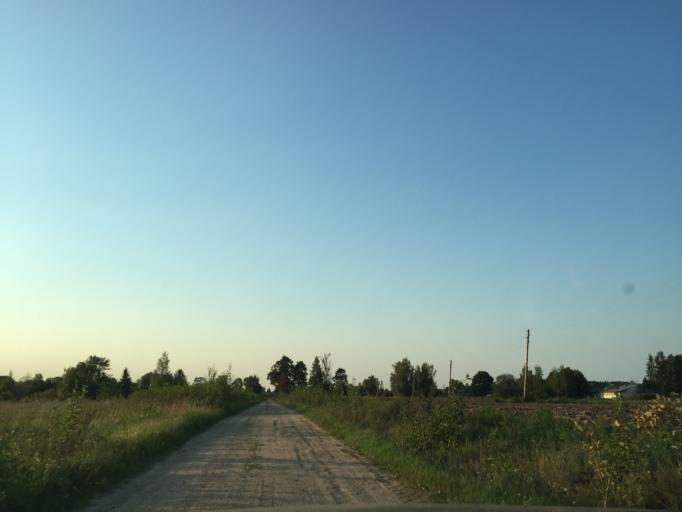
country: LV
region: Limbazu Rajons
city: Limbazi
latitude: 57.5689
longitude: 24.7710
